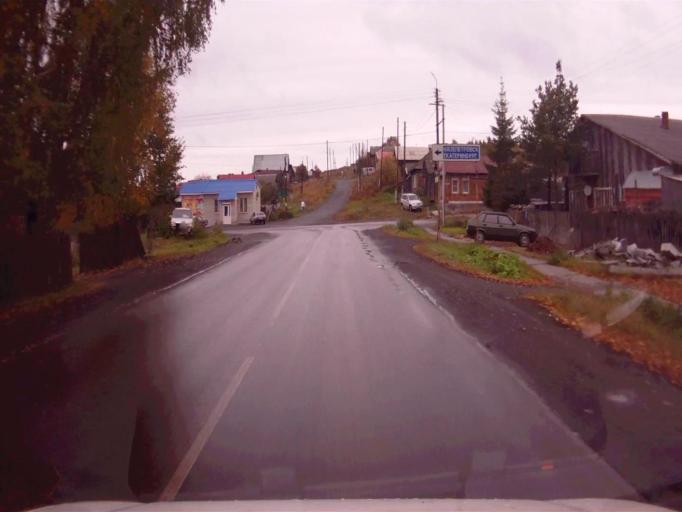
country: RU
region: Chelyabinsk
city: Verkhniy Ufaley
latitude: 56.0580
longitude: 60.2042
